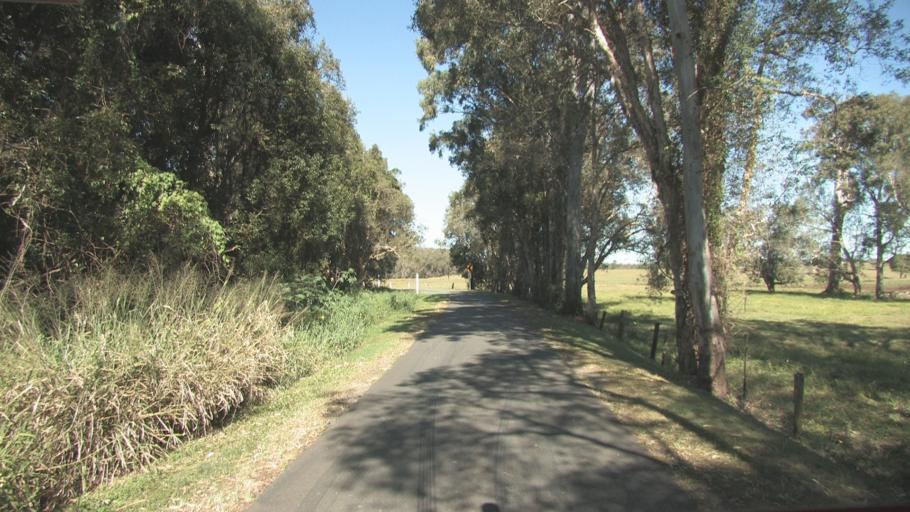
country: AU
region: Queensland
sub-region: Gold Coast
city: Yatala
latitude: -27.6886
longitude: 153.2276
